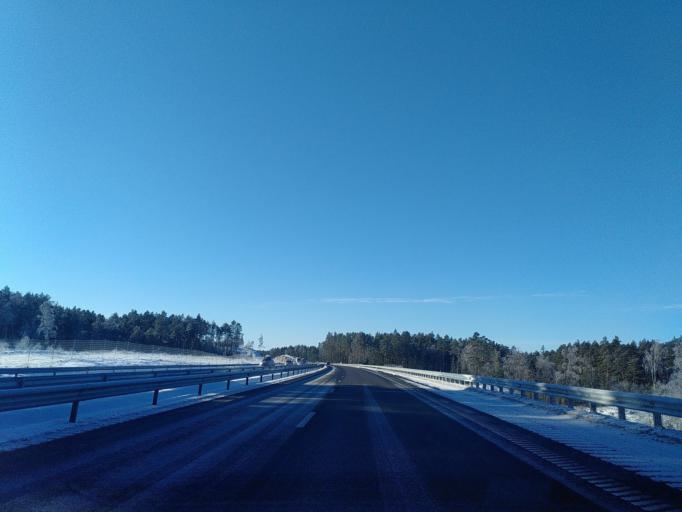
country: SE
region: Vaestra Goetaland
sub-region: Vargarda Kommun
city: Jonstorp
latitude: 57.9908
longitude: 12.7260
